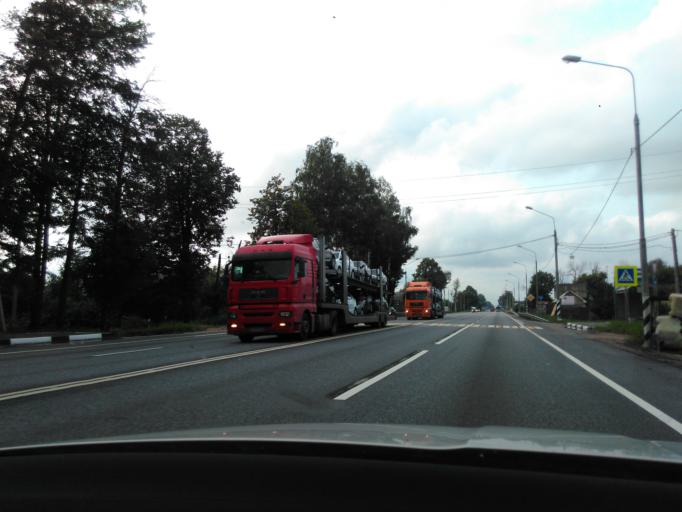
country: RU
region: Tverskaya
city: Zavidovo
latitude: 56.5453
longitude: 36.5182
